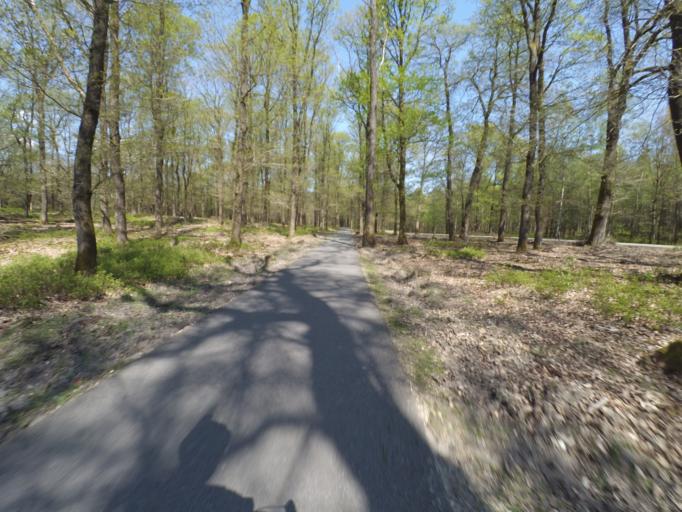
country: NL
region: Gelderland
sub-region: Gemeente Apeldoorn
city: Uddel
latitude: 52.2423
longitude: 5.8262
